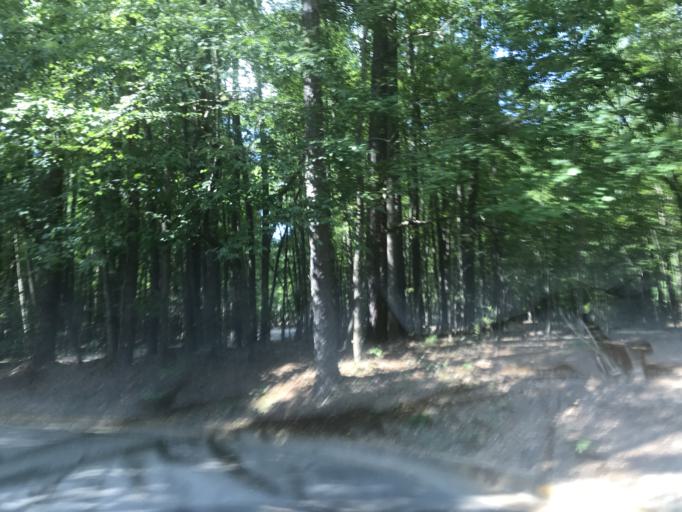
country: US
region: North Carolina
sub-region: Wake County
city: Morrisville
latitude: 35.8723
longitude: -78.7608
